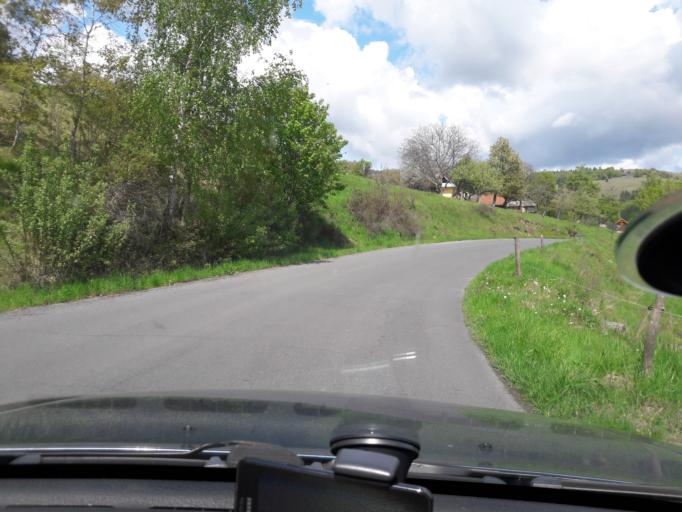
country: SK
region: Banskobystricky
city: Hrinova
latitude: 48.5933
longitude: 19.4817
